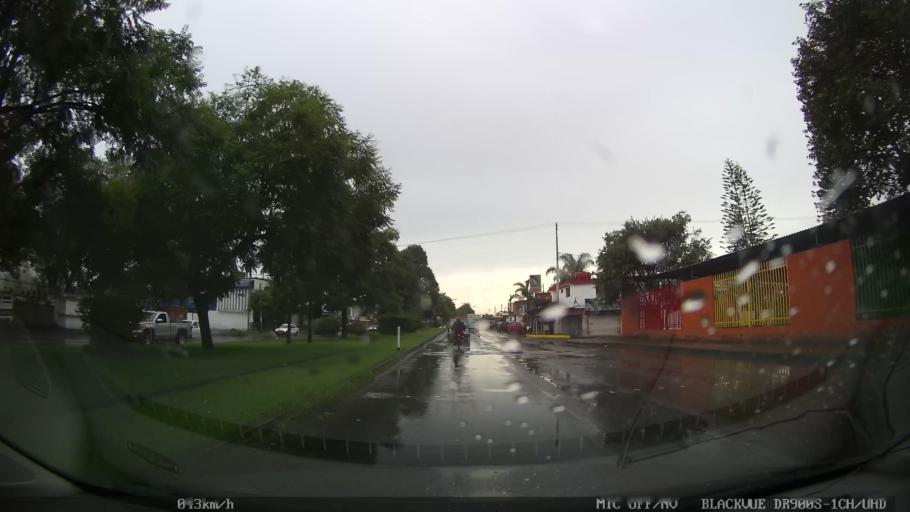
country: MX
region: Michoacan
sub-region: Uruapan
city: Uruapan
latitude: 19.4147
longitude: -102.0254
